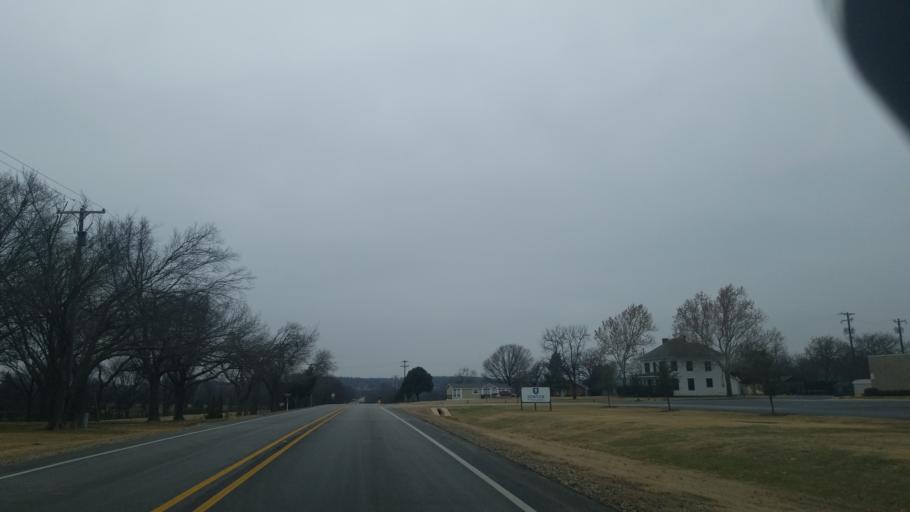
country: US
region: Texas
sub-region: Denton County
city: Argyle
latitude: 33.1591
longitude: -97.1419
